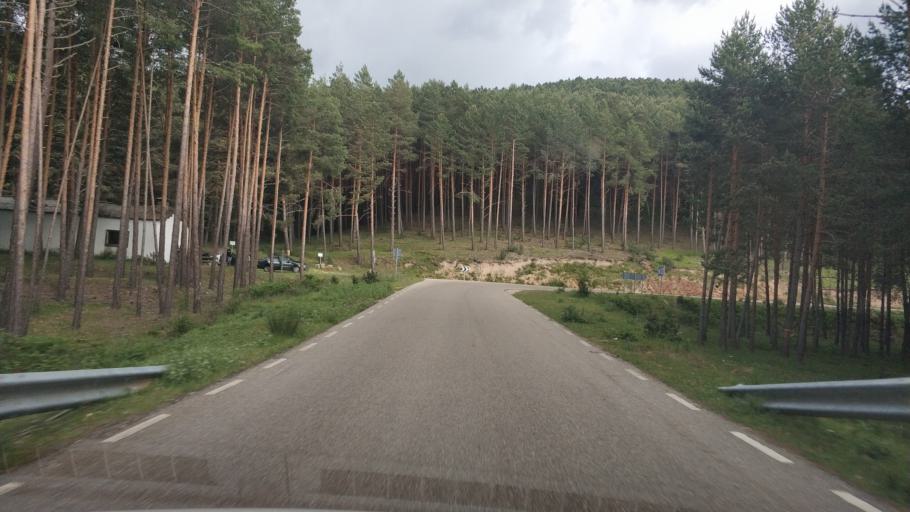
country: ES
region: Castille and Leon
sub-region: Provincia de Soria
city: San Leonardo de Yague
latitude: 41.8528
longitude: -3.0687
